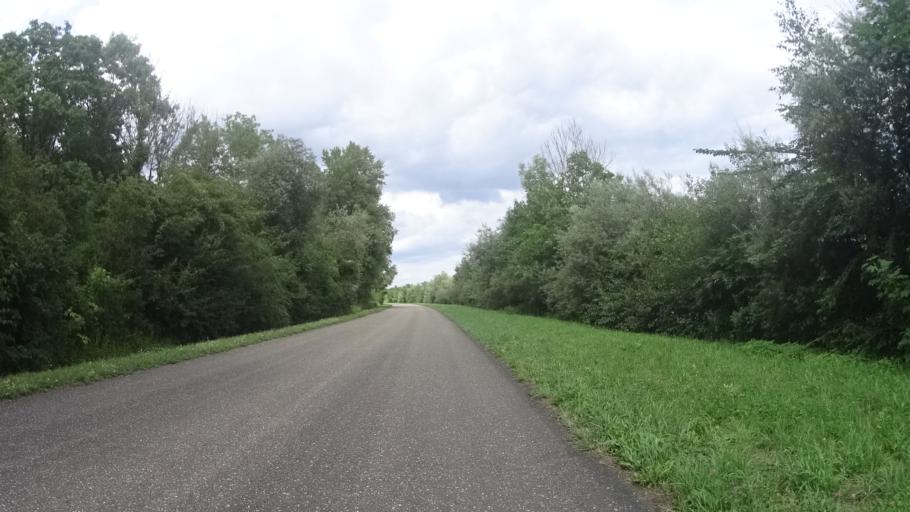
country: FR
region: Alsace
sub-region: Departement du Bas-Rhin
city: Drusenheim
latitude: 48.7237
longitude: 7.9626
